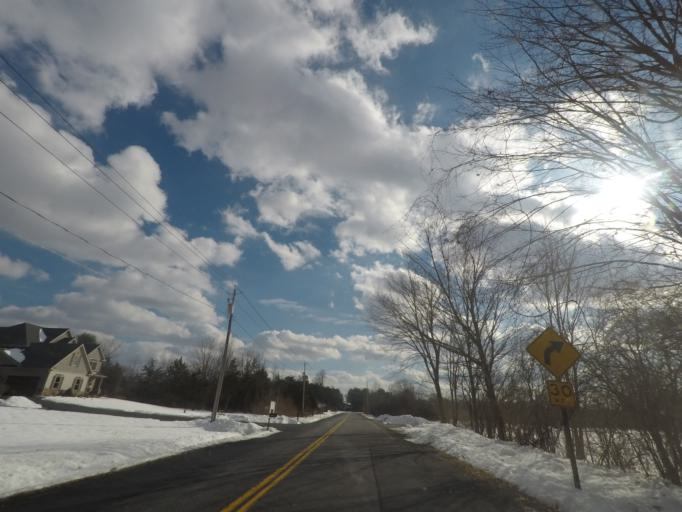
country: US
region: New York
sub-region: Schenectady County
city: Niskayuna
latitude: 42.8319
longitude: -73.8640
